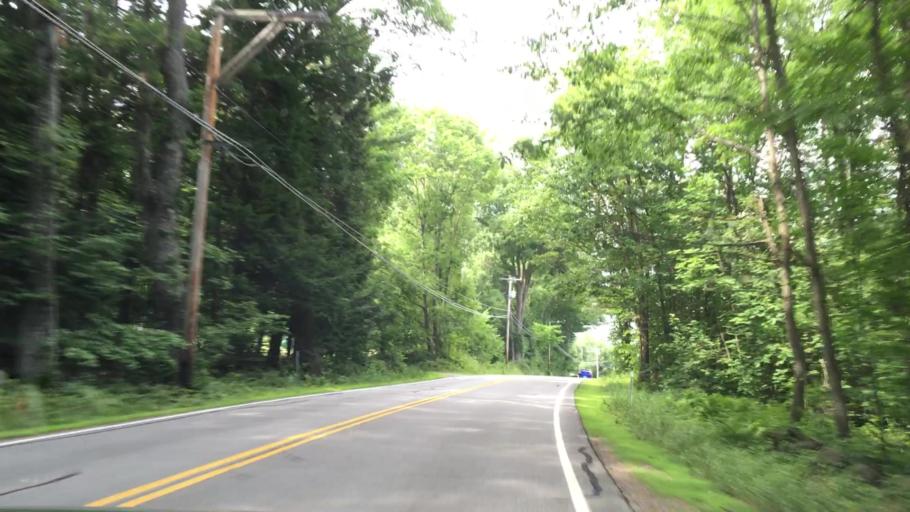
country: US
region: New Hampshire
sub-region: Hillsborough County
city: Antrim
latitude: 43.0389
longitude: -71.9359
